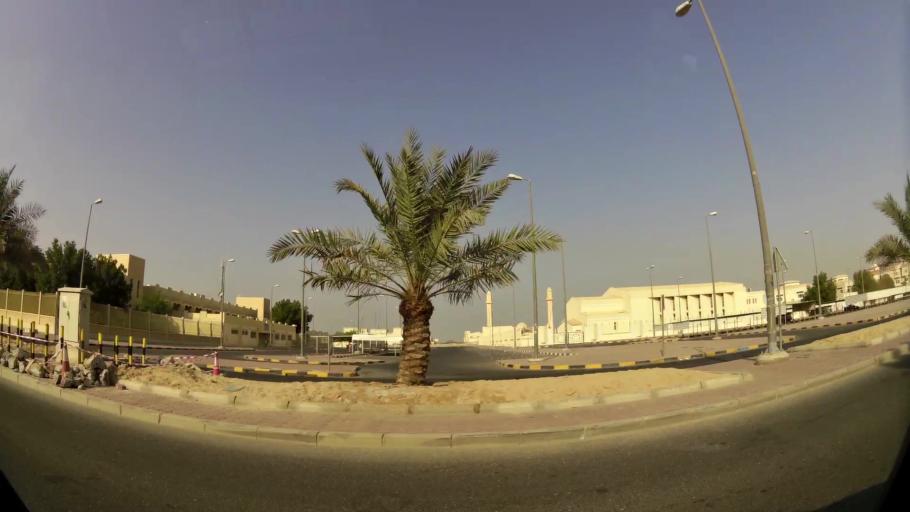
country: KW
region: Al Asimah
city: Ar Rabiyah
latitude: 29.2998
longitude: 47.7997
